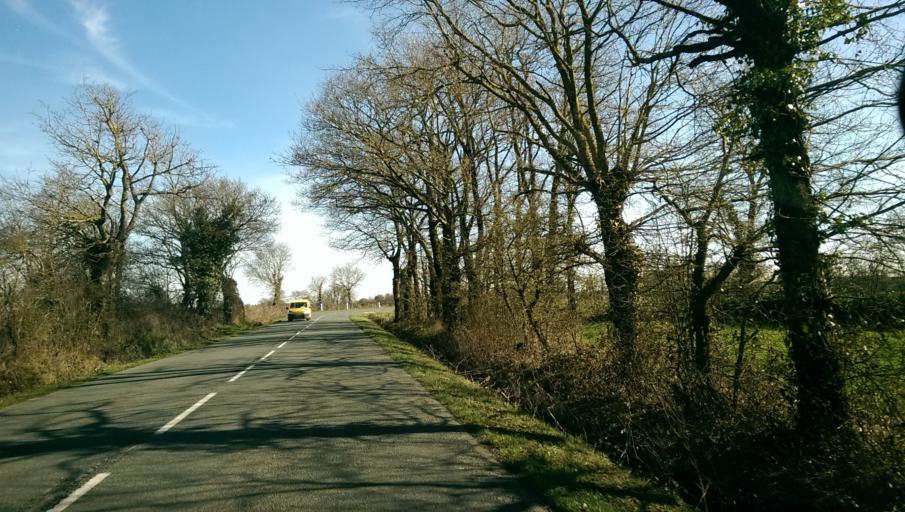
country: FR
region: Pays de la Loire
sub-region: Departement de la Vendee
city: Beaurepaire
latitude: 46.9310
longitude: -1.1037
